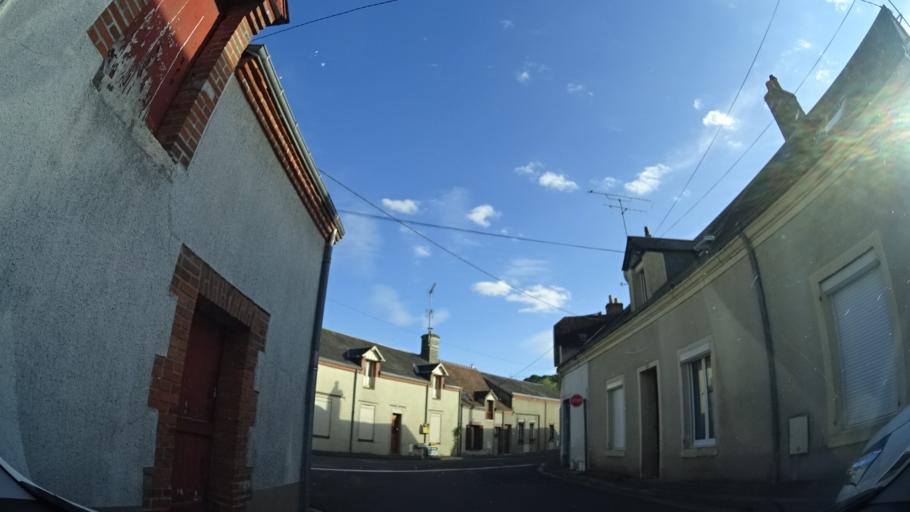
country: FR
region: Centre
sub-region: Departement du Loir-et-Cher
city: Moree
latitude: 47.9018
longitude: 1.2345
